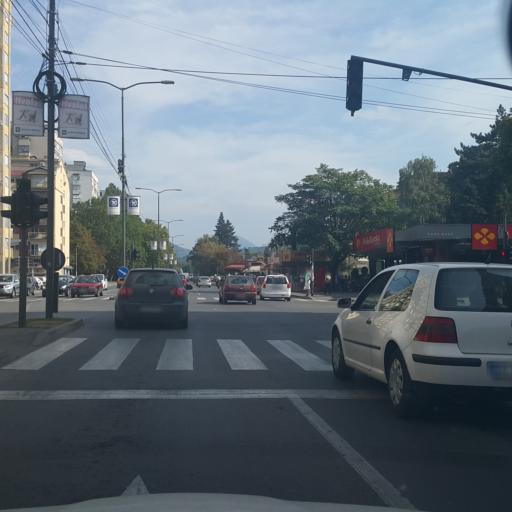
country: RS
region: Central Serbia
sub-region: Nisavski Okrug
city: Nis
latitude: 43.3179
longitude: 21.9110
